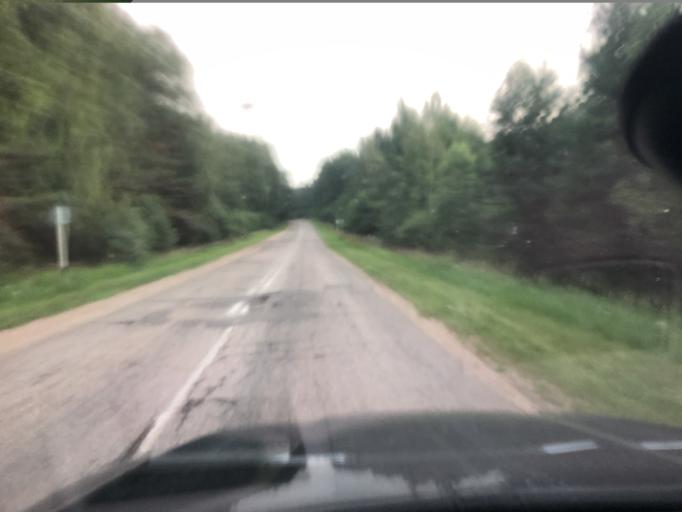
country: RU
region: Jaroslavl
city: Petrovsk
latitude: 57.0001
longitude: 39.0698
